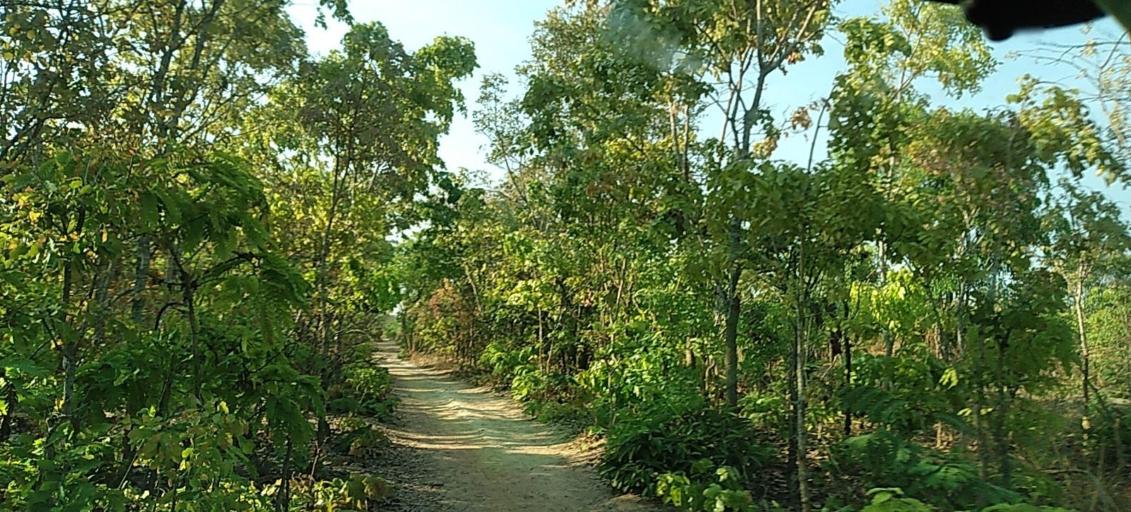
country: ZM
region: North-Western
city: Kalengwa
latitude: -13.1774
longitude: 25.0397
